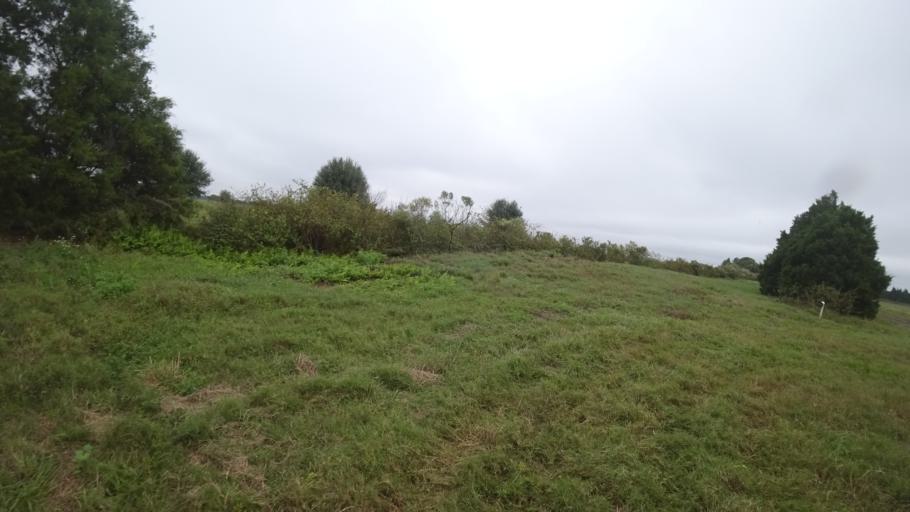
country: US
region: Florida
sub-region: Sarasota County
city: Warm Mineral Springs
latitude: 27.3096
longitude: -82.1497
